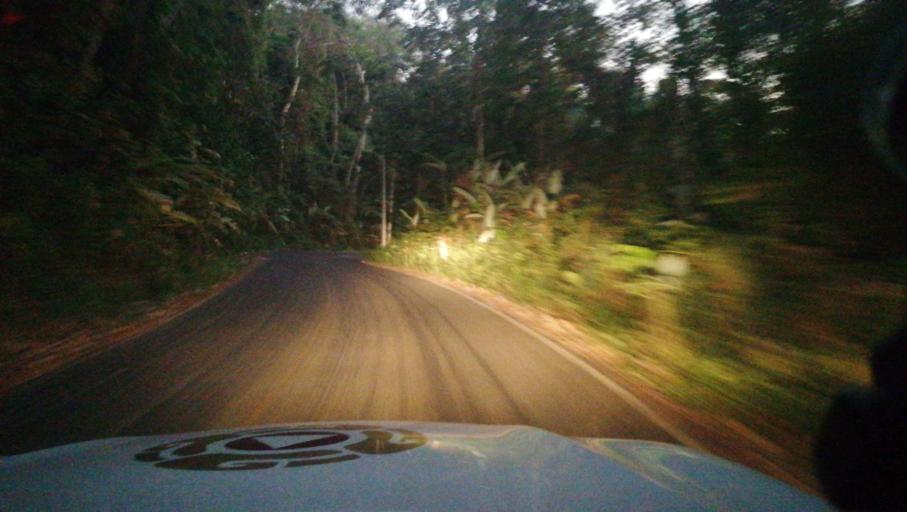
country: MX
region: Chiapas
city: Veinte de Noviembre
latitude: 14.9651
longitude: -92.2524
